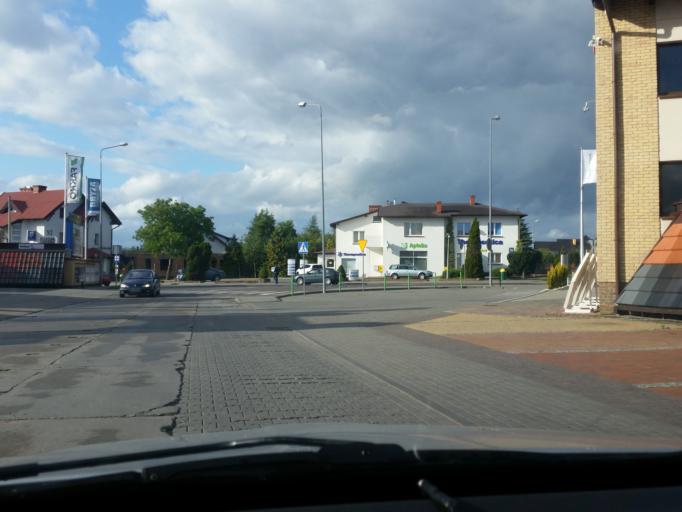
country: PL
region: Pomeranian Voivodeship
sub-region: Powiat chojnicki
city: Chojnice
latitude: 53.7049
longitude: 17.5459
